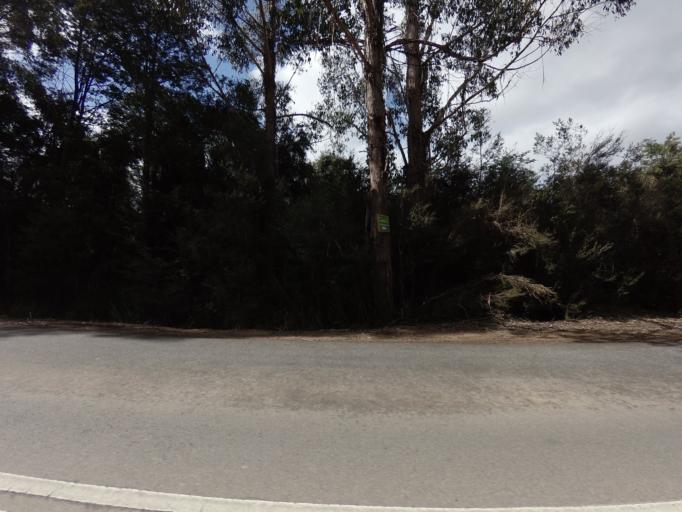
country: AU
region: Tasmania
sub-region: Huon Valley
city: Geeveston
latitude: -43.3550
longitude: 146.9581
